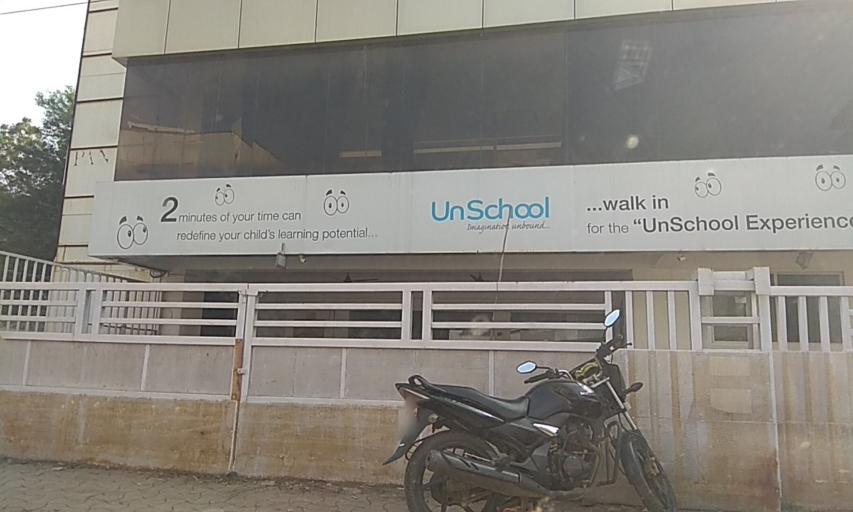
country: IN
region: Maharashtra
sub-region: Pune Division
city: Pimpri
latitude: 18.5622
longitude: 73.7804
